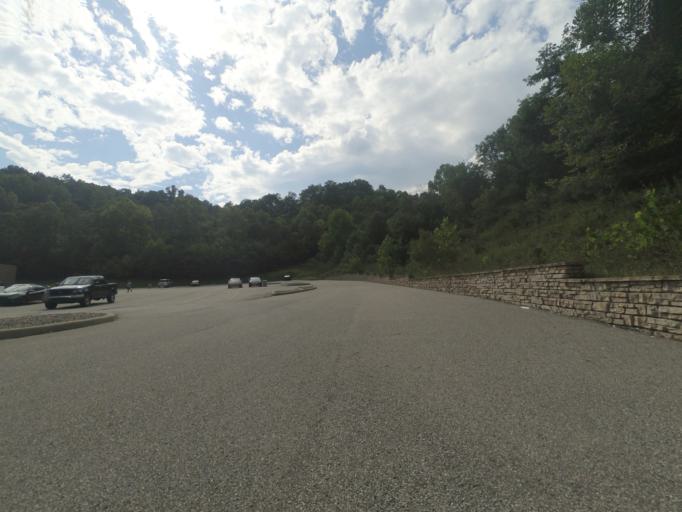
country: US
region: West Virginia
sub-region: Cabell County
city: Huntington
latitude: 38.3896
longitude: -82.4572
